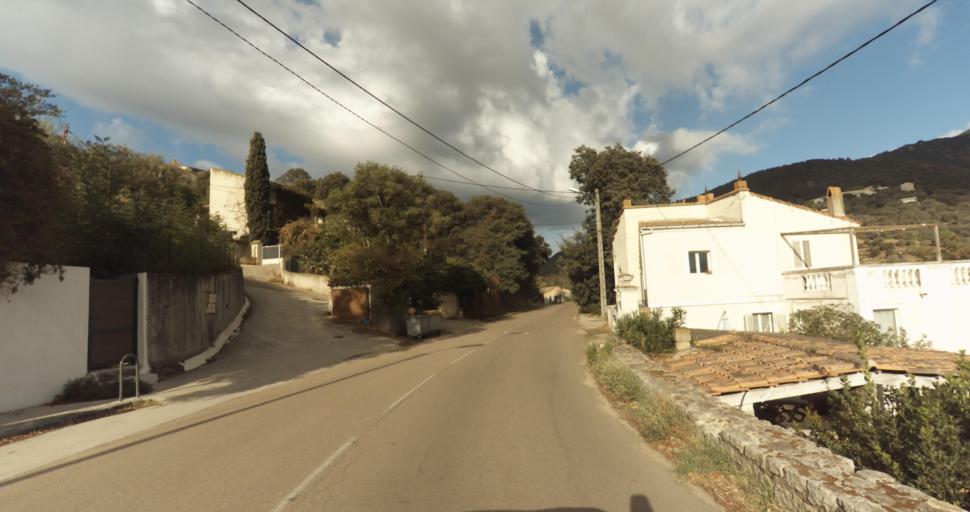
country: FR
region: Corsica
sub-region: Departement de la Corse-du-Sud
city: Ajaccio
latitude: 41.9312
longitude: 8.7235
